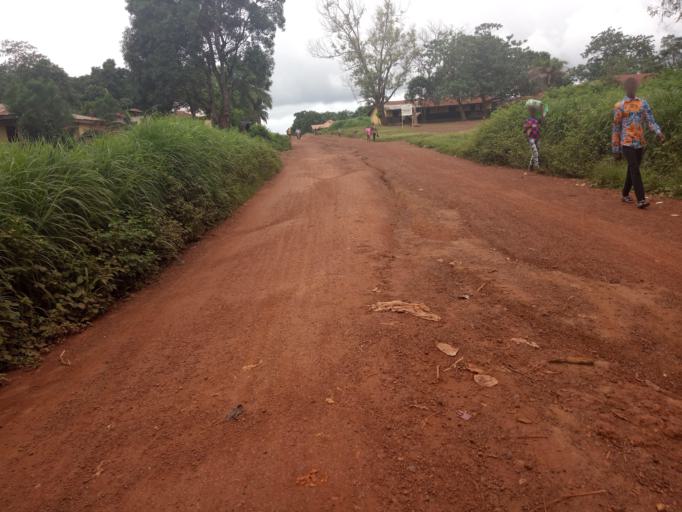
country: SL
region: Northern Province
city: Kamakwie
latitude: 9.4986
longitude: -12.2474
